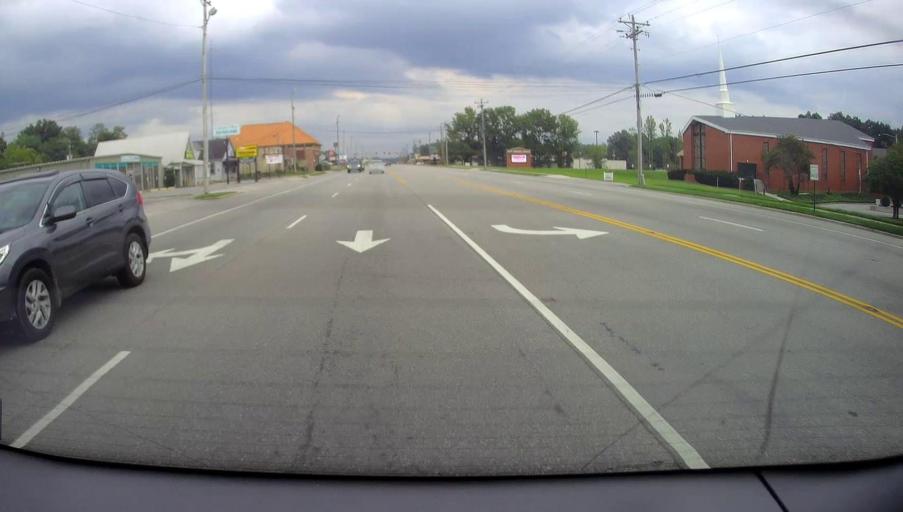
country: US
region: Tennessee
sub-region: Coffee County
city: Manchester
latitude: 35.4736
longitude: -86.0780
